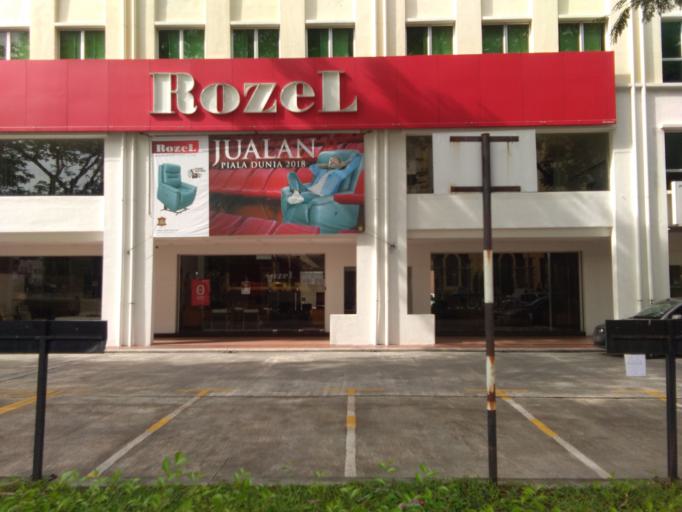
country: MY
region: Perak
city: Ipoh
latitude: 4.6000
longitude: 101.0925
